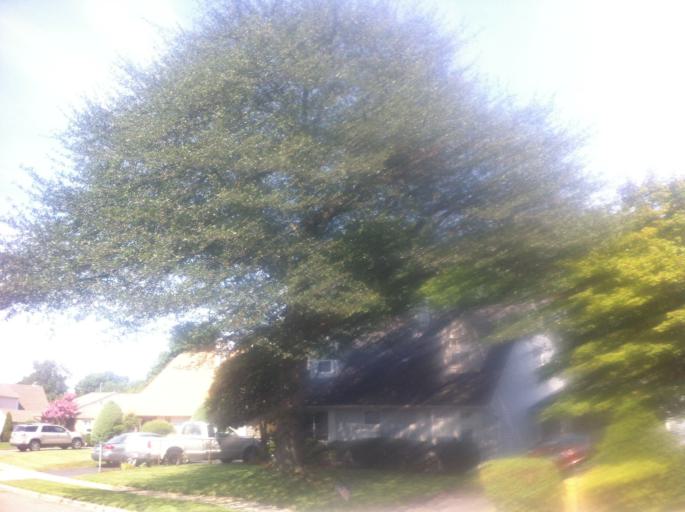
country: US
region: New York
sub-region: Nassau County
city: Locust Valley
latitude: 40.8551
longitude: -73.6026
